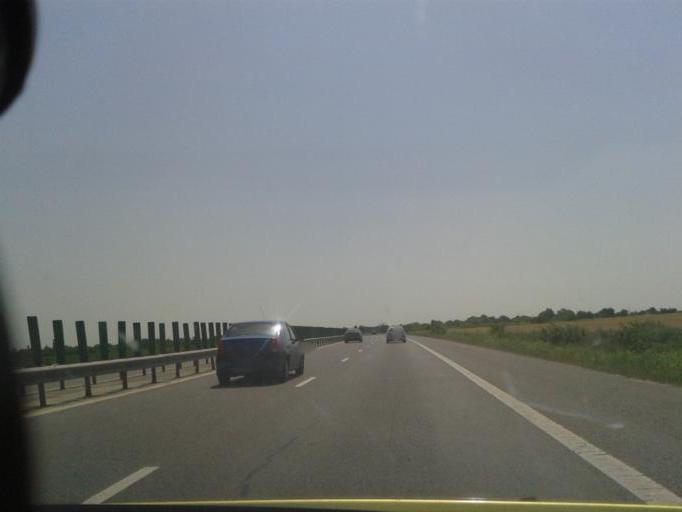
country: RO
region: Calarasi
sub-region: Comuna Sarulesti
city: Sarulesti-Gara
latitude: 44.4428
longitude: 26.6407
